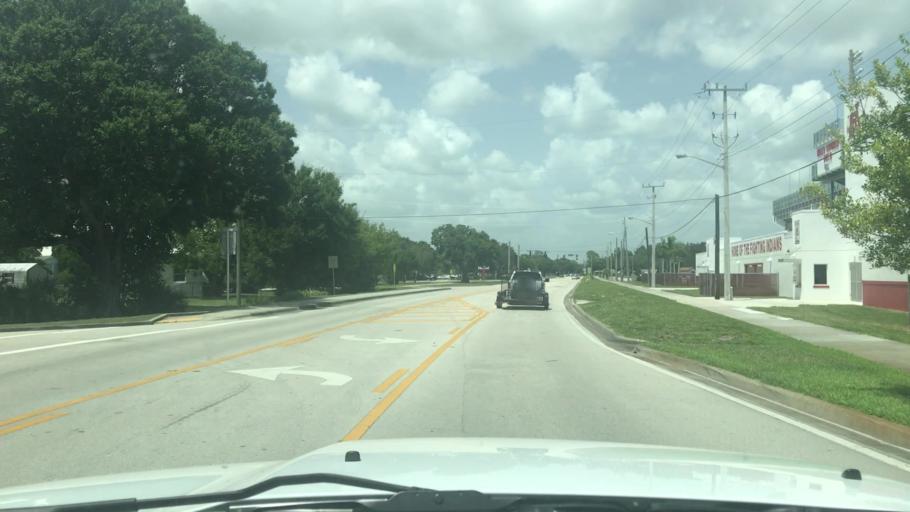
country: US
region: Florida
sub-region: Indian River County
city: Vero Beach
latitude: 27.6309
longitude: -80.4005
